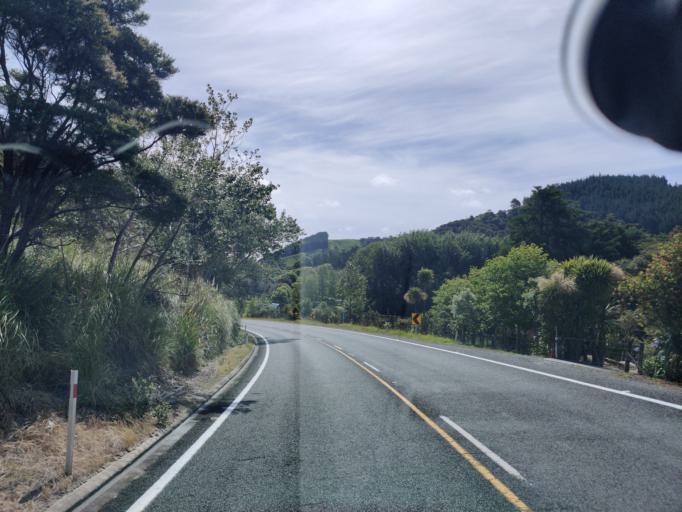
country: NZ
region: Northland
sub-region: Far North District
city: Kaitaia
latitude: -35.4855
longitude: 173.4347
